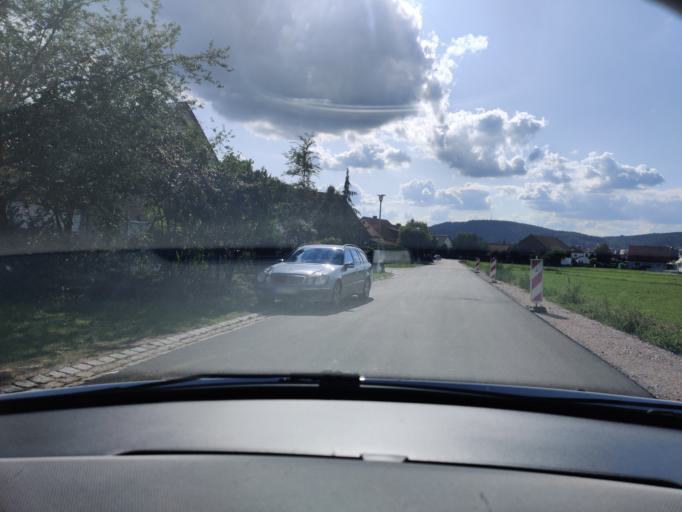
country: DE
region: Bavaria
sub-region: Upper Palatinate
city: Nabburg
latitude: 49.4463
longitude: 12.1987
